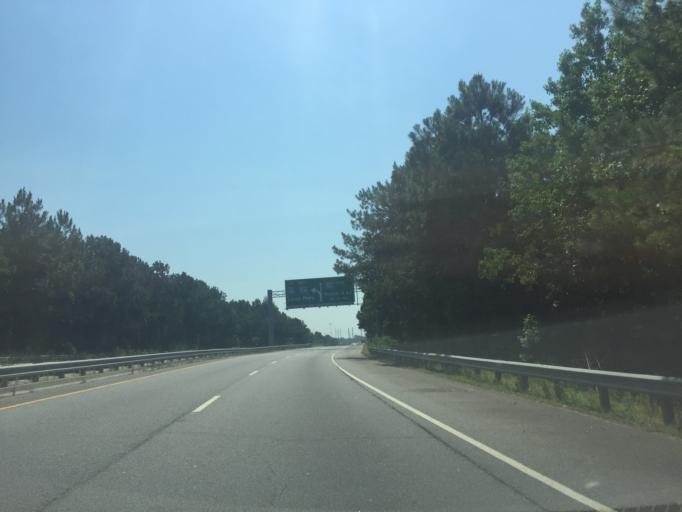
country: US
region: Georgia
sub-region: Chatham County
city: Savannah
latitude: 32.0425
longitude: -81.1586
